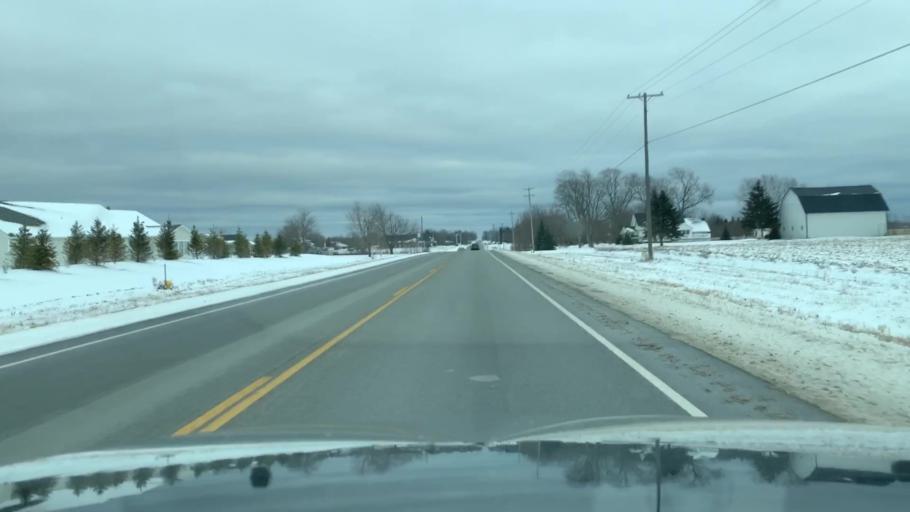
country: US
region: Michigan
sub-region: Ottawa County
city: Zeeland
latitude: 42.8122
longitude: -85.9588
